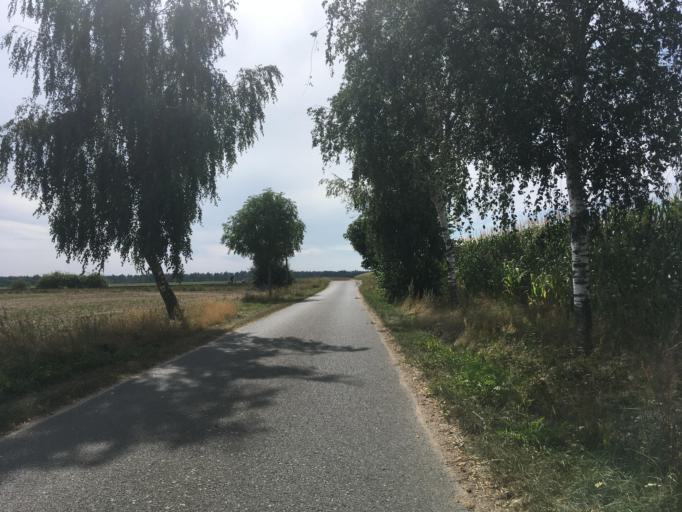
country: DE
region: Saxony-Anhalt
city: Pretzsch
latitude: 51.6960
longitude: 12.8145
